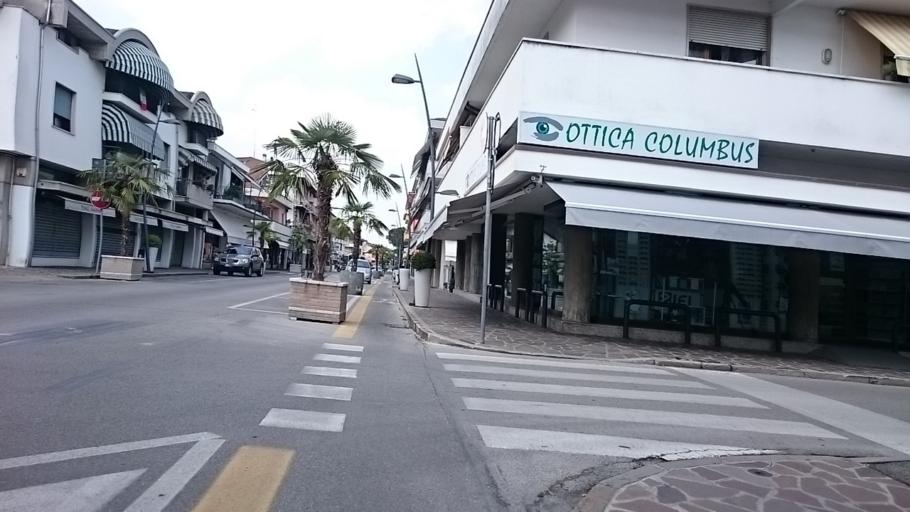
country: IT
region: Veneto
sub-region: Provincia di Padova
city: Abano Terme
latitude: 45.3499
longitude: 11.7874
